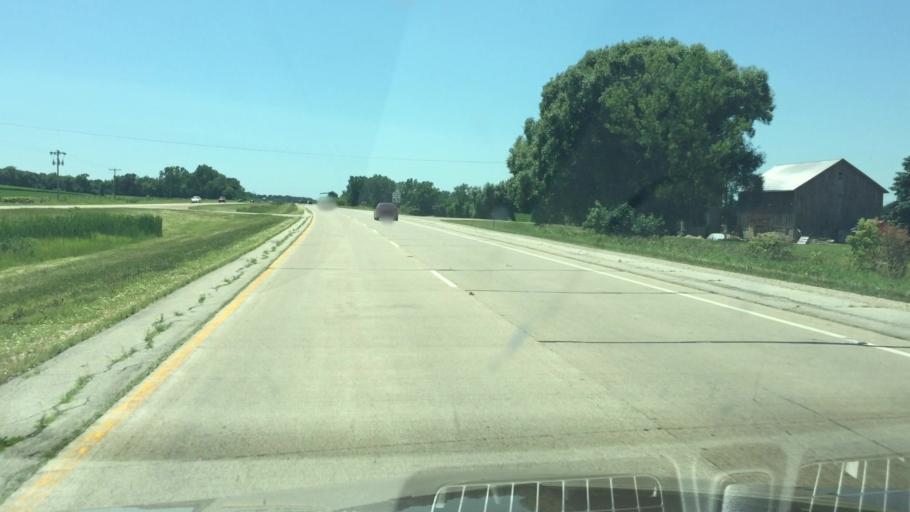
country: US
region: Wisconsin
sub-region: Columbia County
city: Columbus
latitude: 43.3776
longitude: -88.9639
